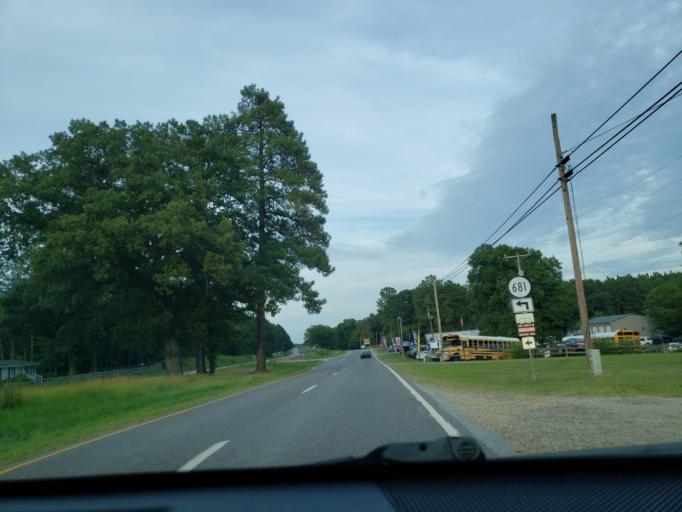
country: US
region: Virginia
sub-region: Brunswick County
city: Lawrenceville
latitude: 36.7442
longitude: -77.8790
